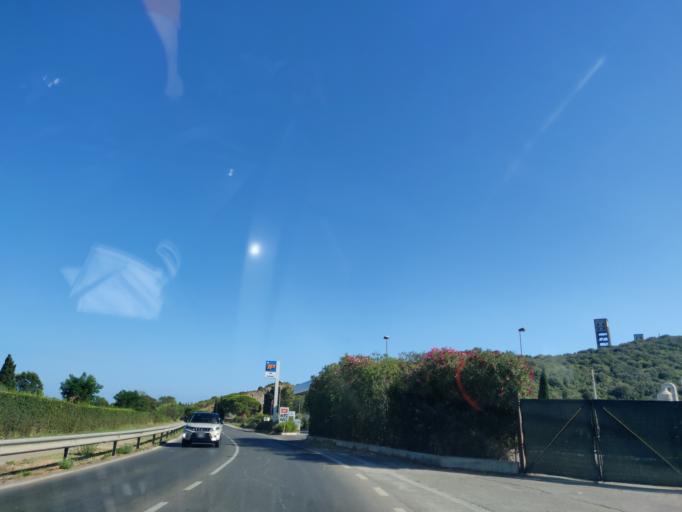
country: IT
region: Tuscany
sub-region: Provincia di Grosseto
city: Porto Ercole
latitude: 42.4262
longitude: 11.1972
